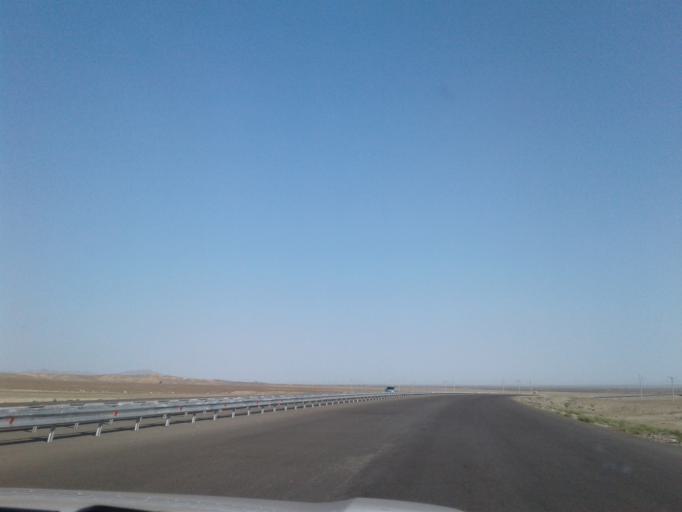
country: TM
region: Balkan
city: Serdar
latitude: 38.7254
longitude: 56.7799
